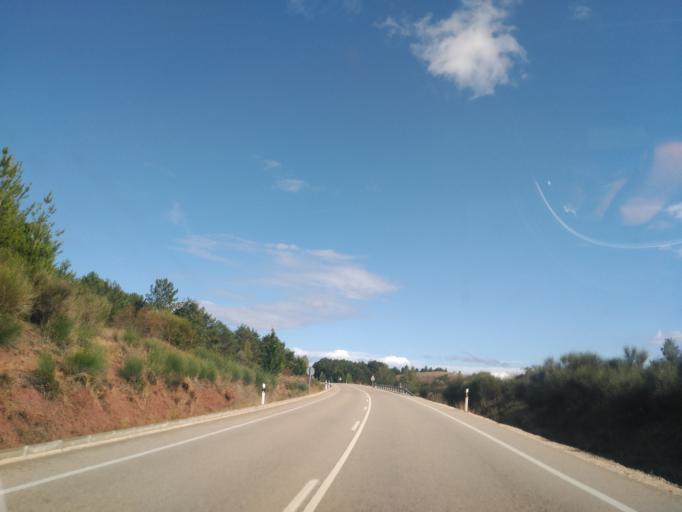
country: ES
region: Castille and Leon
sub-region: Provincia de Burgos
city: Cabezon de la Sierra
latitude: 41.8901
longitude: -3.2500
